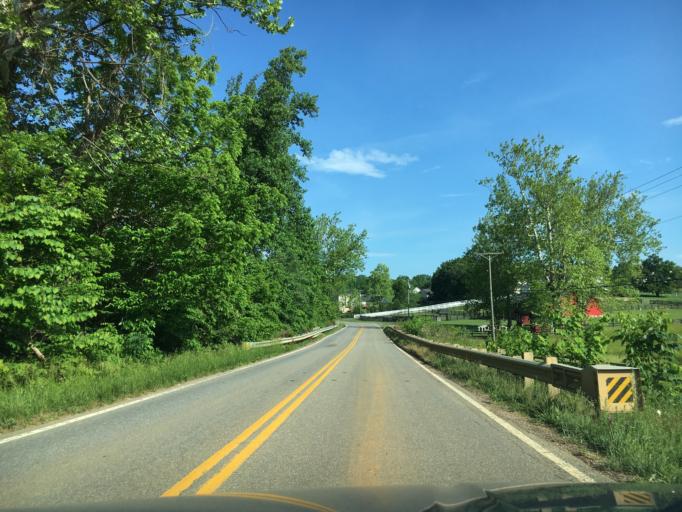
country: US
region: Virginia
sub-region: Campbell County
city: Rustburg
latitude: 37.3110
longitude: -79.1717
